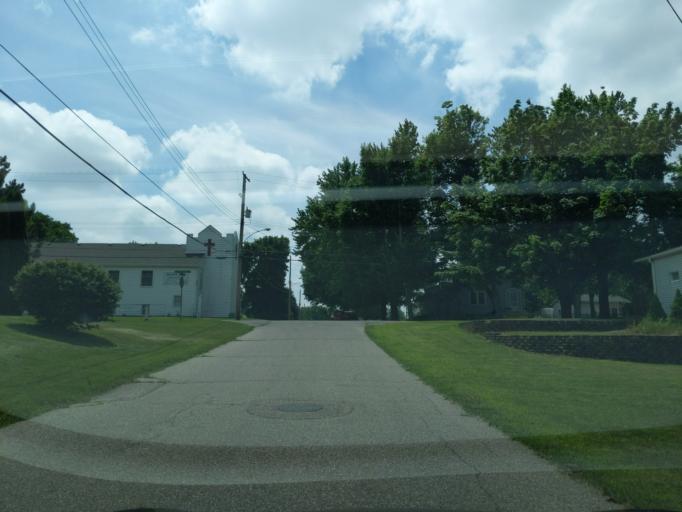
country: US
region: Michigan
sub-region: Ingham County
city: Lansing
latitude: 42.7682
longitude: -84.5483
